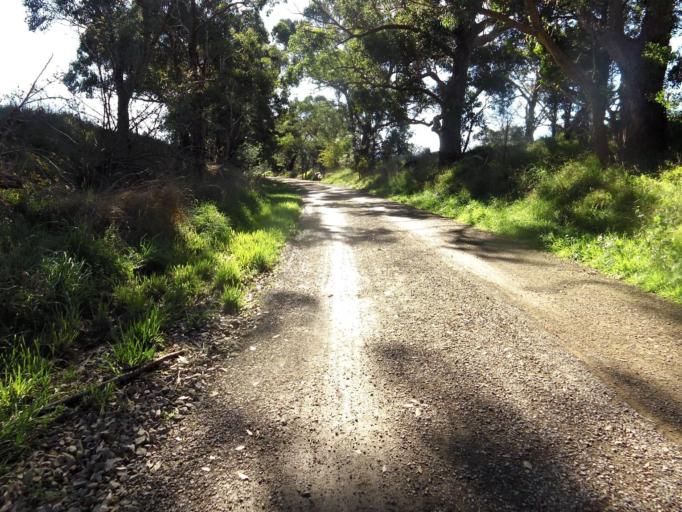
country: AU
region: Victoria
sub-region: Yarra Ranges
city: Lilydale
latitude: -37.7306
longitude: 145.3718
